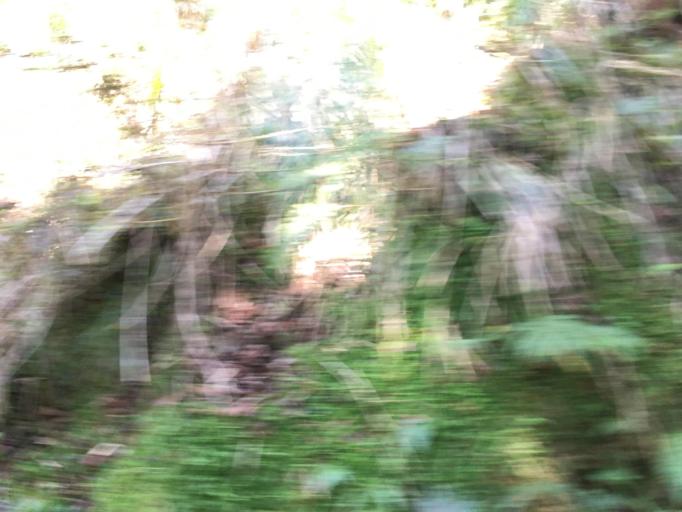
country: TW
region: Taiwan
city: Daxi
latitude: 24.5574
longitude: 121.3979
